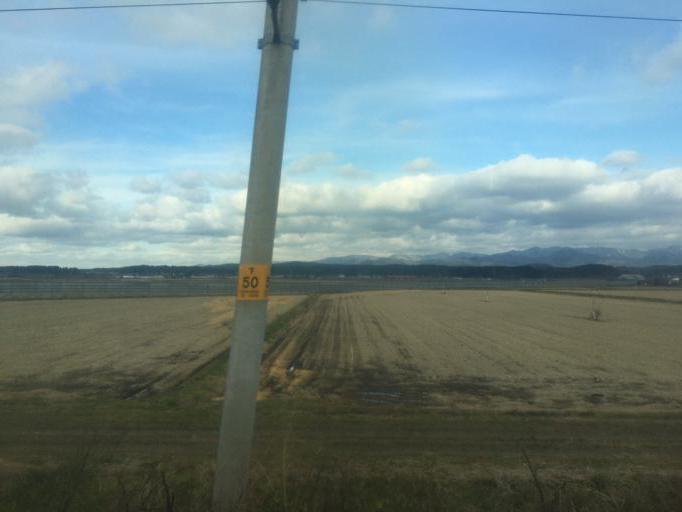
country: JP
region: Akita
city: Noshiromachi
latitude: 40.2127
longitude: 140.1536
